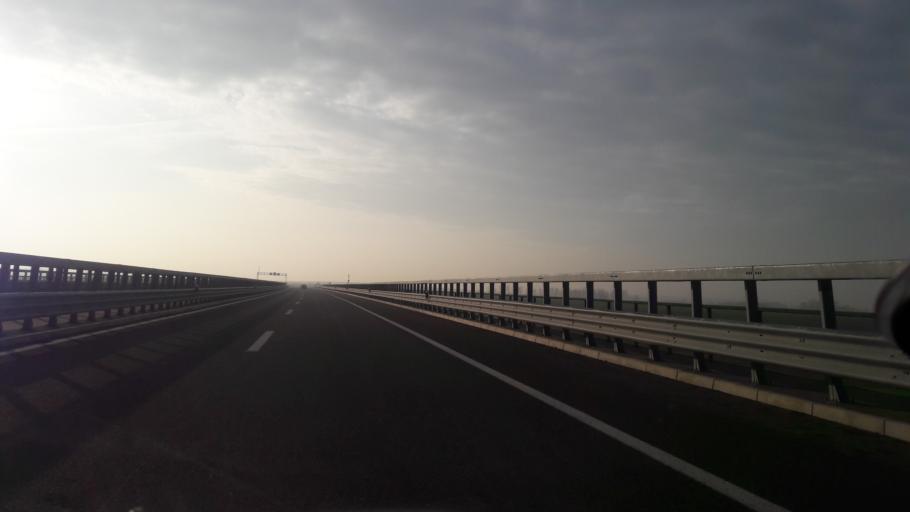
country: HR
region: Osjecko-Baranjska
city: Gorjani
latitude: 45.3658
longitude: 18.3966
